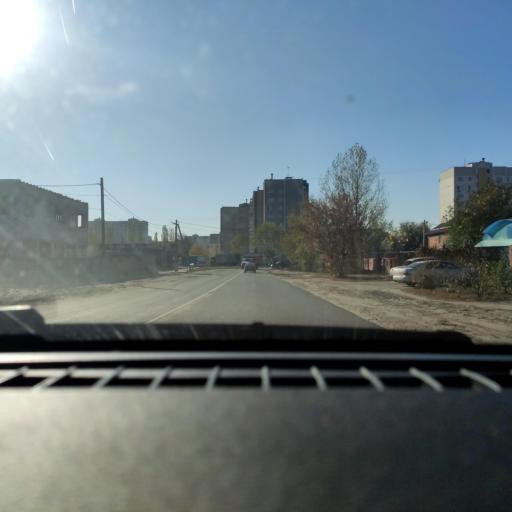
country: RU
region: Voronezj
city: Somovo
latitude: 51.7399
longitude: 39.2922
